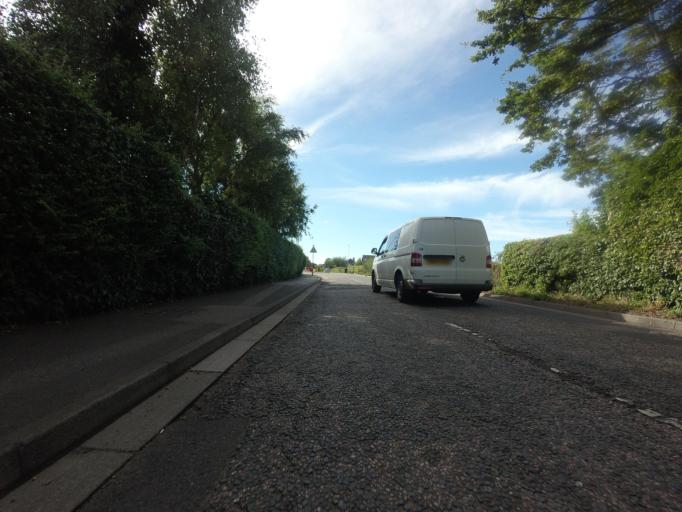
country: GB
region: England
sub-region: Kent
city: Herne Bay
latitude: 51.3692
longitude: 1.1706
